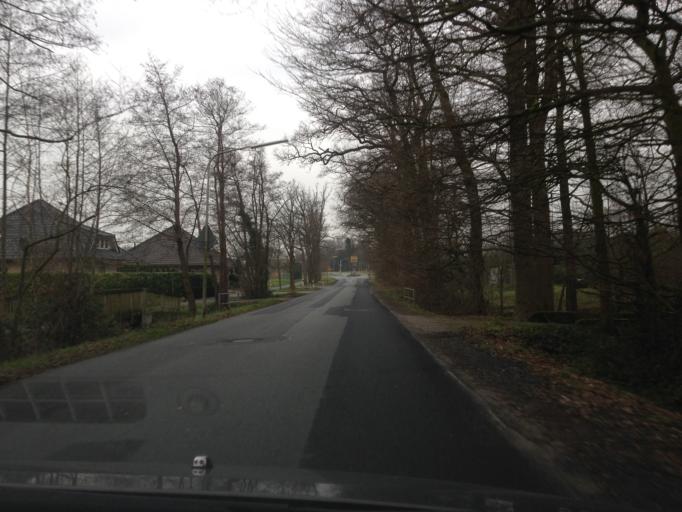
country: DE
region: Lower Saxony
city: Bad Bentheim
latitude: 52.2960
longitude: 7.1362
